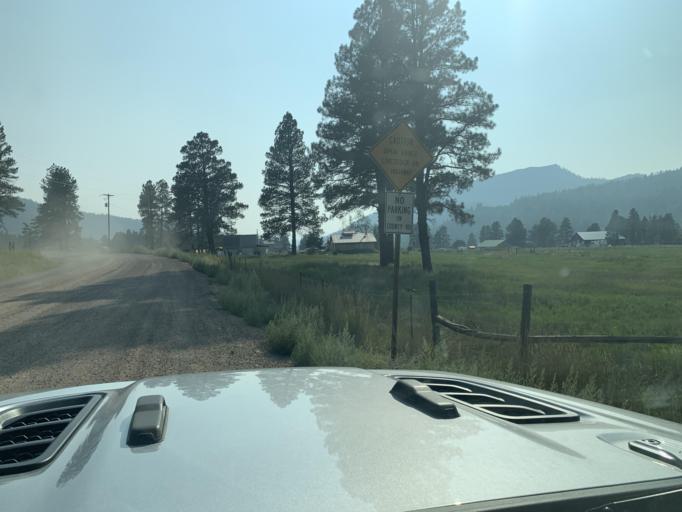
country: US
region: Colorado
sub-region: Archuleta County
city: Pagosa Springs
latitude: 37.2229
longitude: -107.2095
